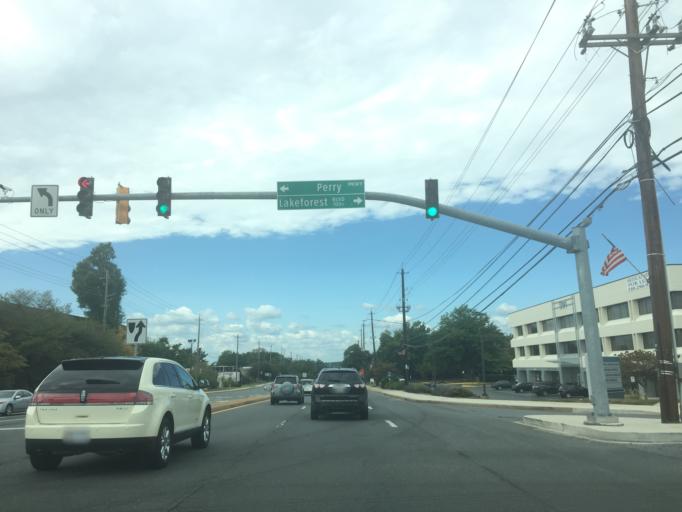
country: US
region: Maryland
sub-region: Montgomery County
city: Gaithersburg
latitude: 39.1501
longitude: -77.2089
